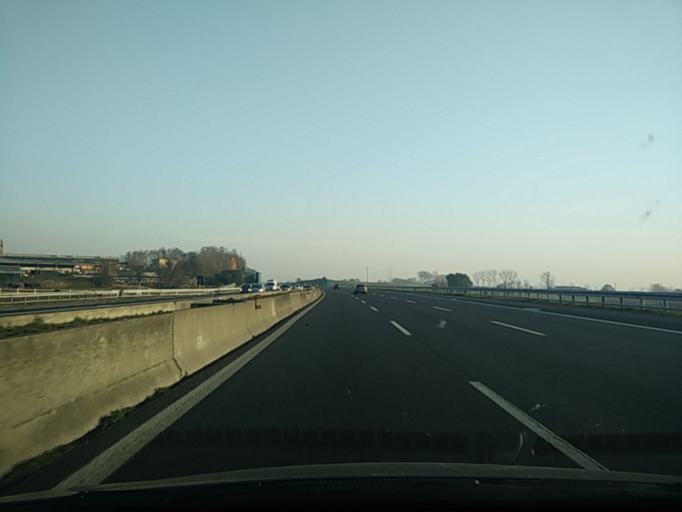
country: IT
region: Lombardy
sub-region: Provincia di Brescia
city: Villa Pedergnano
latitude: 45.5832
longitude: 9.9839
